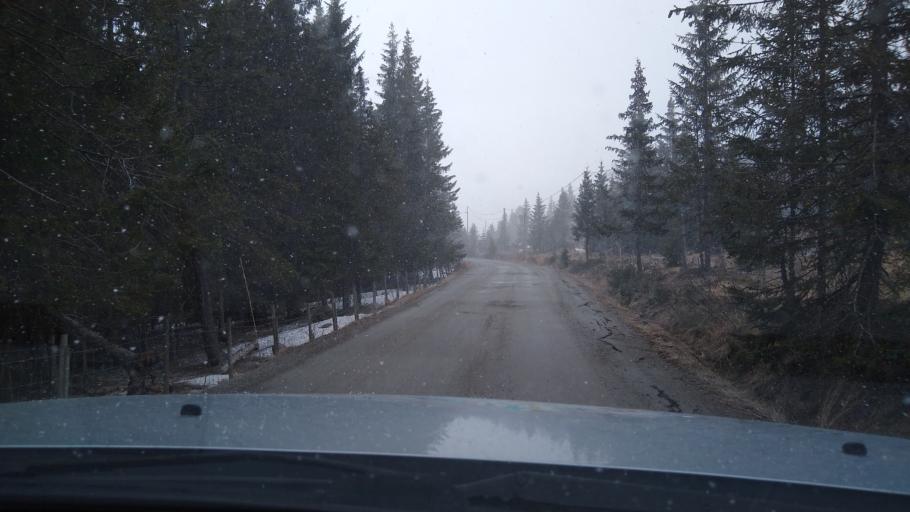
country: NO
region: Oppland
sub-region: Oyer
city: Tretten
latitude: 61.4622
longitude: 10.3428
